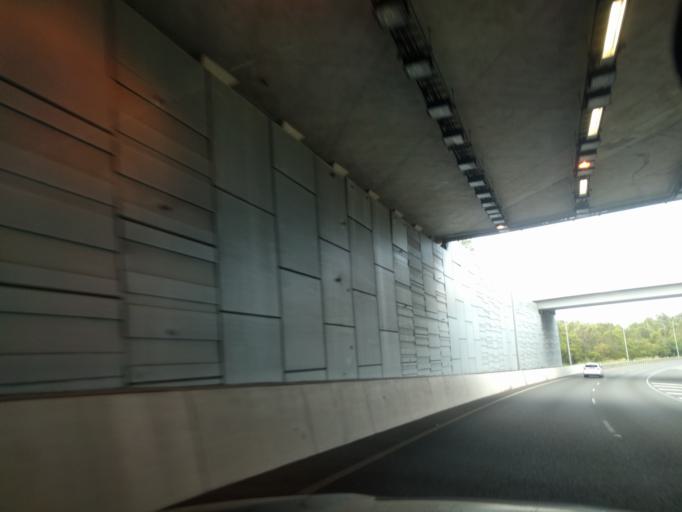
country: AU
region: Queensland
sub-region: Brisbane
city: Wacol
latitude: -27.5778
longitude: 152.9449
